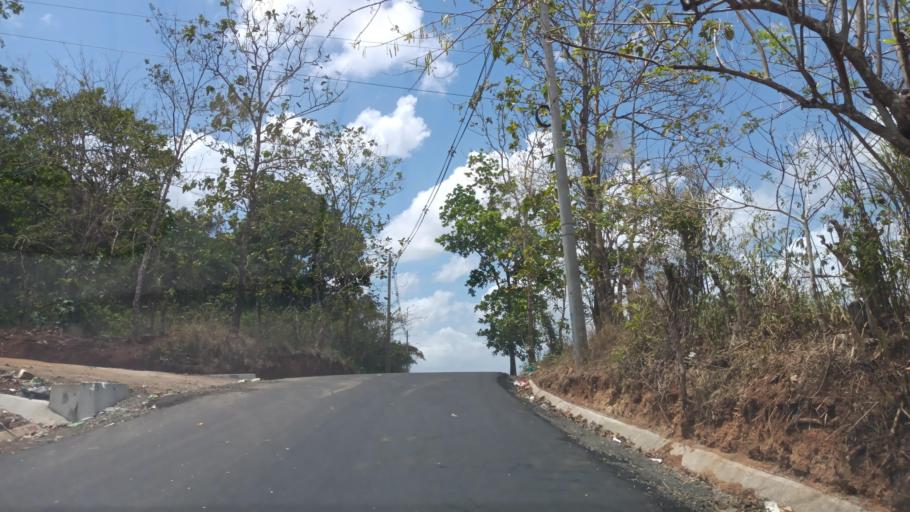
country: PA
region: Panama
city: Alcalde Diaz
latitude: 9.0986
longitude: -79.5684
